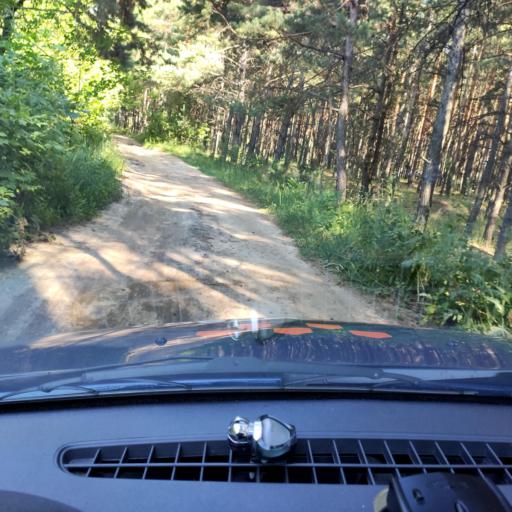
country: RU
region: Voronezj
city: Strelitsa
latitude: 51.6111
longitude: 38.8870
